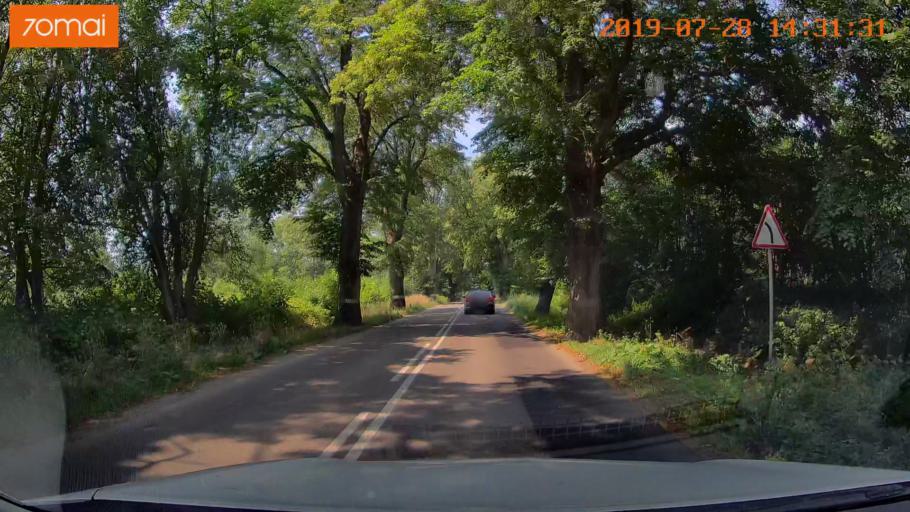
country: RU
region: Kaliningrad
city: Primorsk
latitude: 54.8070
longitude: 20.0505
